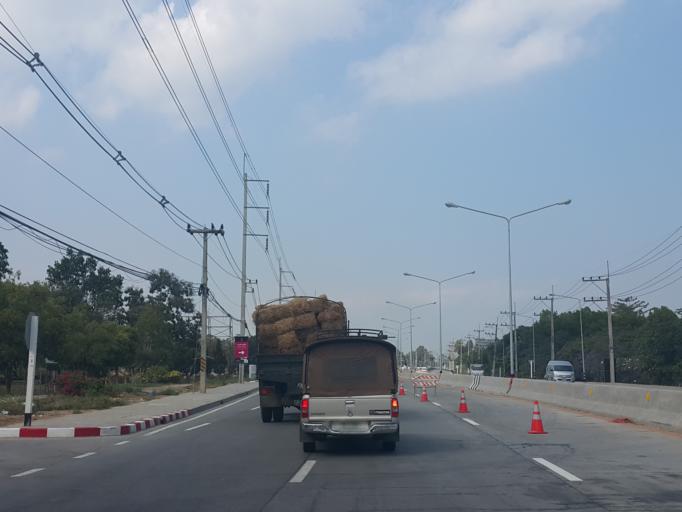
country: TH
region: Chiang Mai
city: Chiang Mai
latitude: 18.8625
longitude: 98.9656
